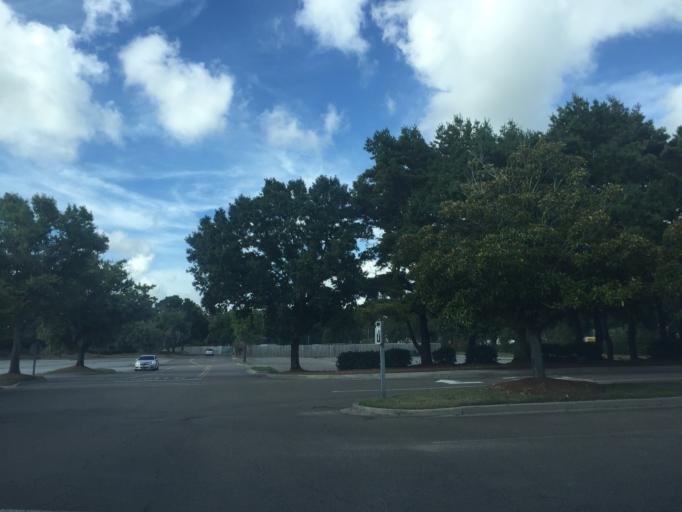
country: US
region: Georgia
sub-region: Chatham County
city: Georgetown
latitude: 31.9823
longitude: -81.1693
